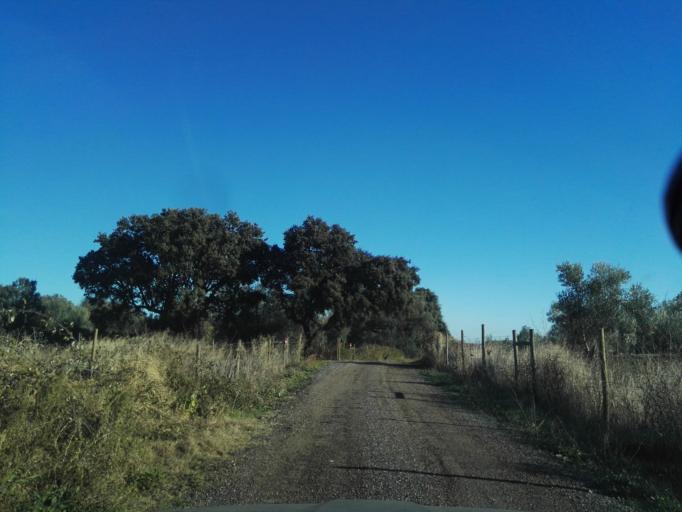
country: PT
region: Portalegre
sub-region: Elvas
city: Elvas
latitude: 38.9190
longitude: -7.1762
